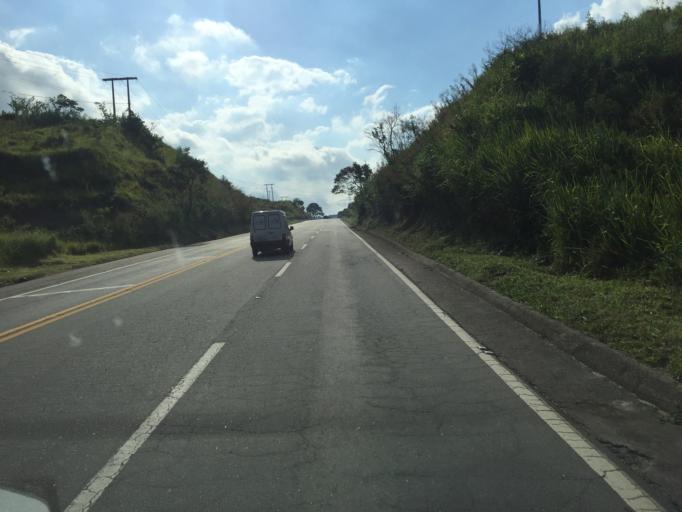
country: BR
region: Sao Paulo
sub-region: Aruja
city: Aruja
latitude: -23.4181
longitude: -46.2839
